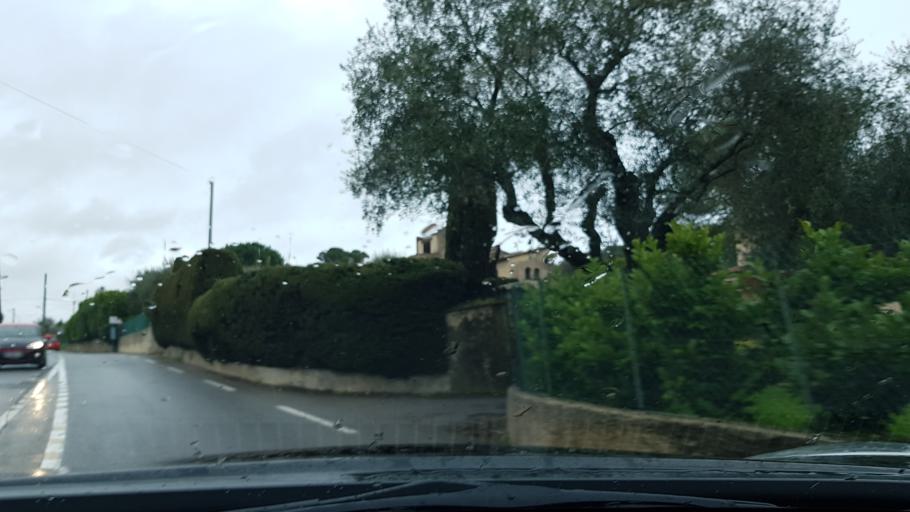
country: FR
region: Provence-Alpes-Cote d'Azur
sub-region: Departement des Alpes-Maritimes
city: Vallauris
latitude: 43.5885
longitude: 7.0525
